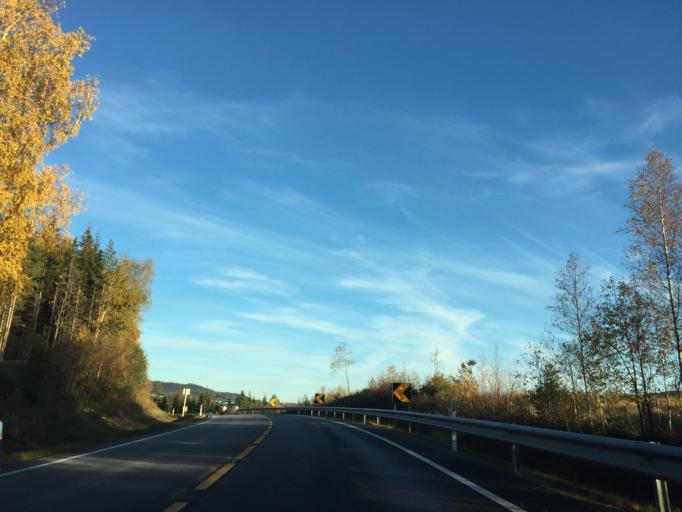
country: NO
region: Hedmark
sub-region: Kongsvinger
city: Spetalen
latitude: 60.2083
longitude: 11.8961
